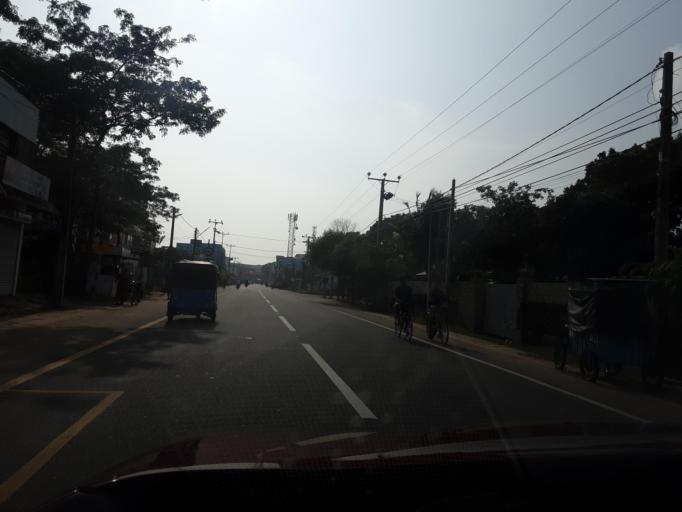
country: LK
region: Northern Province
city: Valvedditturai
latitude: 9.6607
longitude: 80.1662
